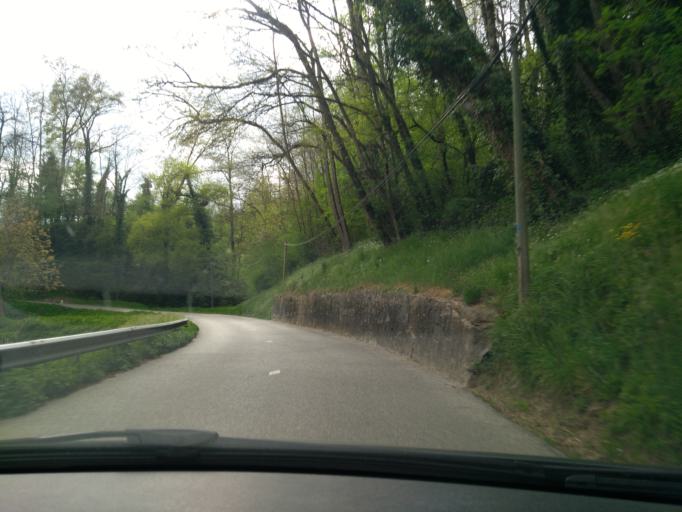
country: FR
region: Rhone-Alpes
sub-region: Departement de la Haute-Savoie
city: Rumilly
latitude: 45.8459
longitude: 5.9183
